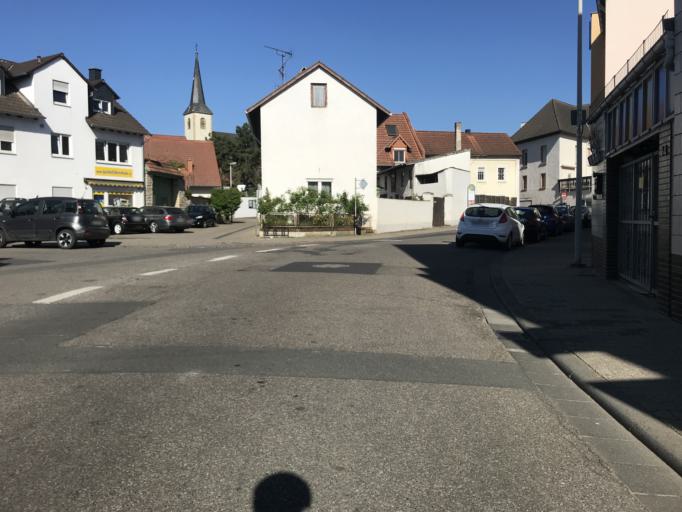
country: DE
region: Rheinland-Pfalz
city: Harxheim
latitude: 49.9130
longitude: 8.2463
